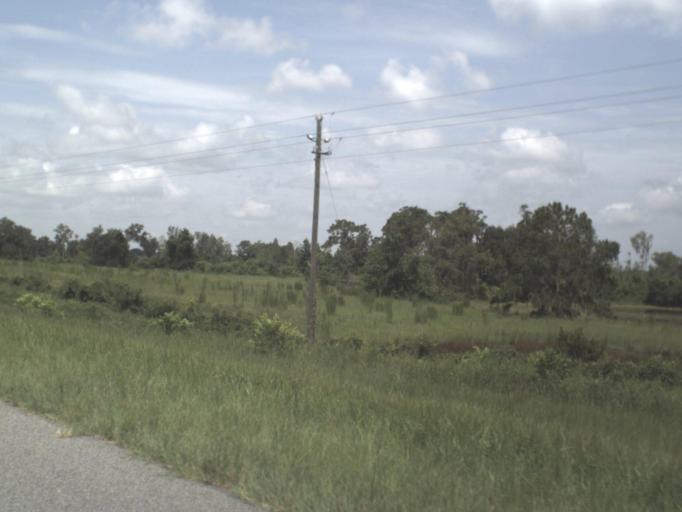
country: US
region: Florida
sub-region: Madison County
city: Madison
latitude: 30.4783
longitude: -83.5552
